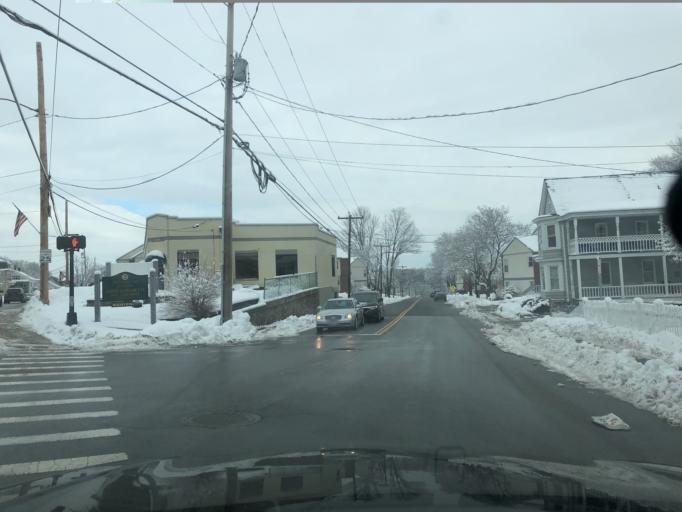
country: US
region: New Hampshire
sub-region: Strafford County
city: Somersworth
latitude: 43.2588
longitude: -70.8670
